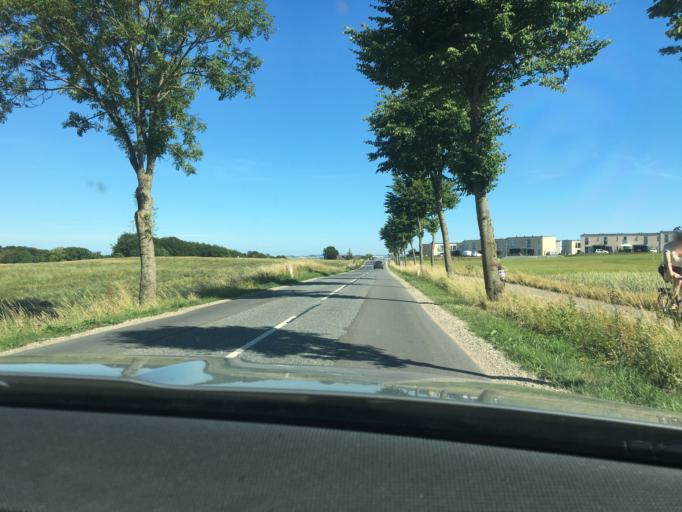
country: DK
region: Central Jutland
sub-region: Syddjurs Kommune
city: Hornslet
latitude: 56.3035
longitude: 10.3576
